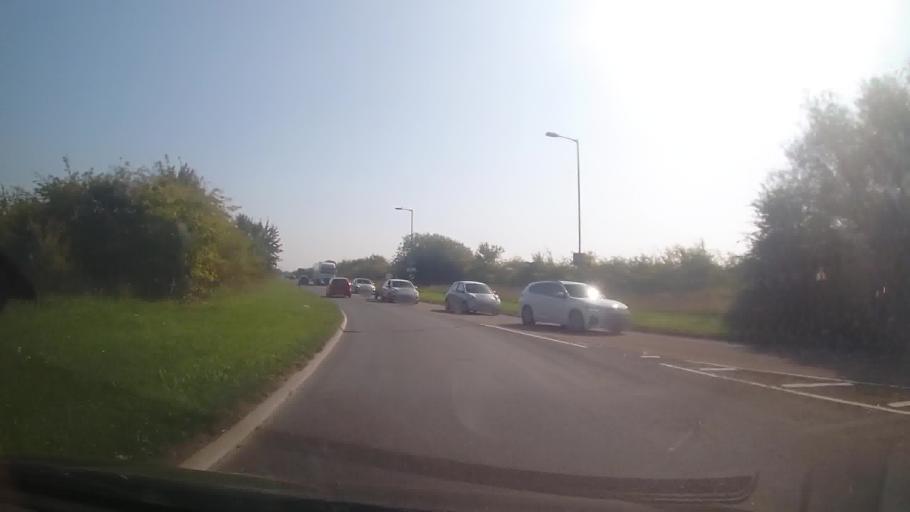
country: GB
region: England
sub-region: Worcestershire
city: Pershore
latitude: 52.1289
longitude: -2.0463
